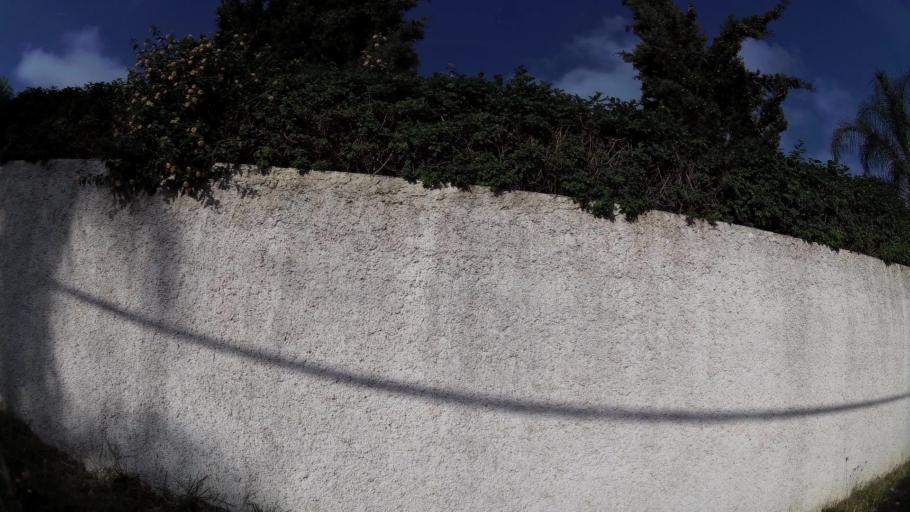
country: MA
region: Rabat-Sale-Zemmour-Zaer
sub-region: Rabat
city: Rabat
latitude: 33.9561
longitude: -6.8454
